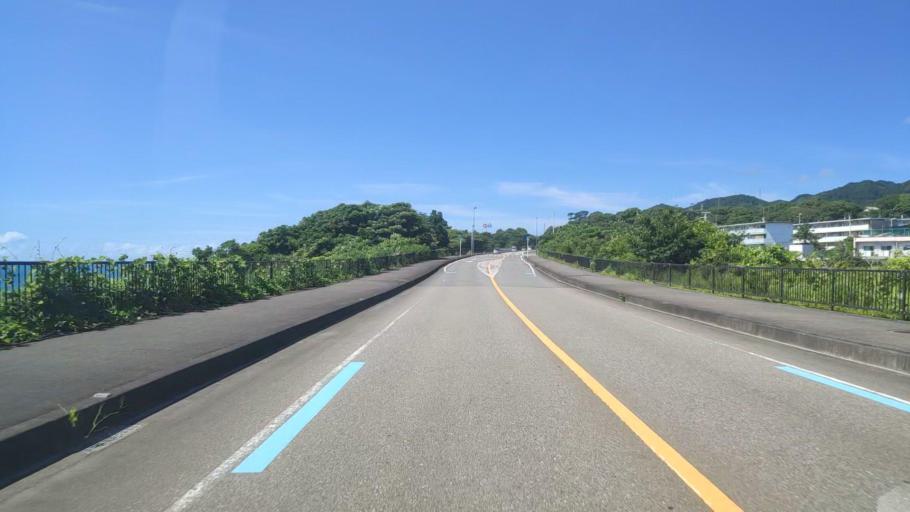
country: JP
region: Wakayama
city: Shingu
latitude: 33.7125
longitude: 135.9993
